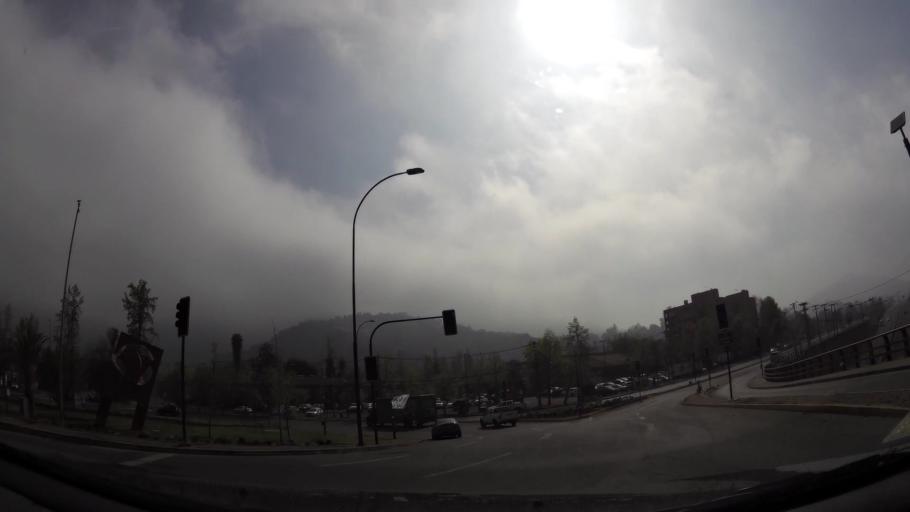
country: CL
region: Santiago Metropolitan
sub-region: Provincia de Santiago
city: Villa Presidente Frei, Nunoa, Santiago, Chile
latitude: -33.3775
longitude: -70.5696
